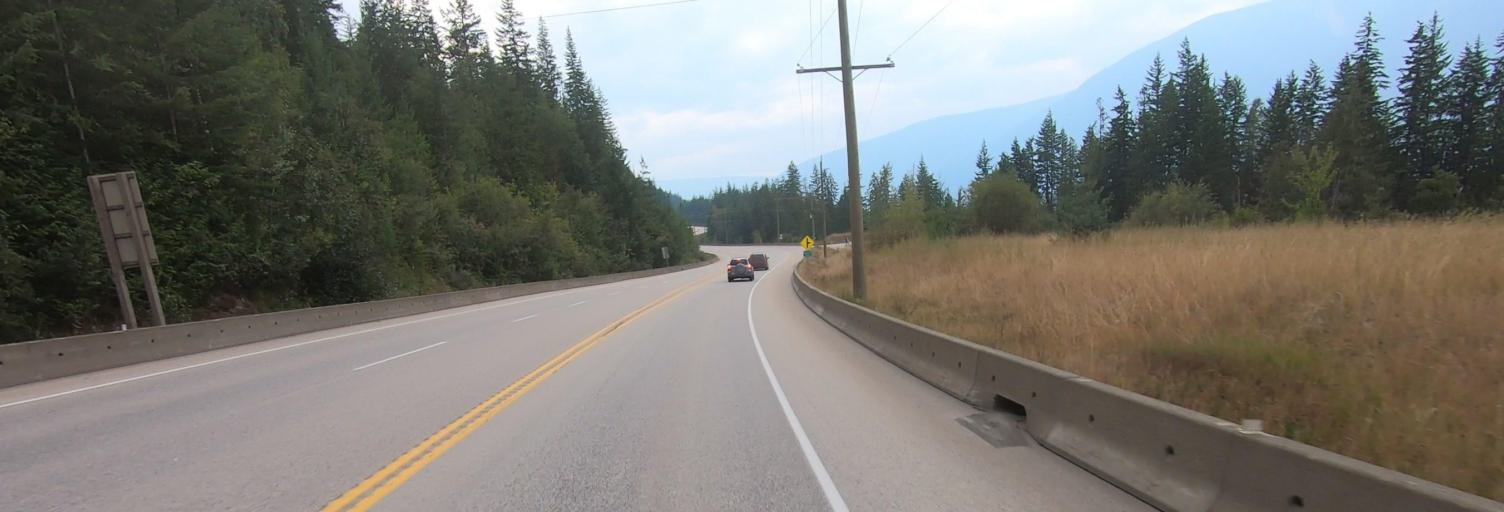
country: CA
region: British Columbia
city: Sicamous
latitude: 50.7888
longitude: -119.0865
